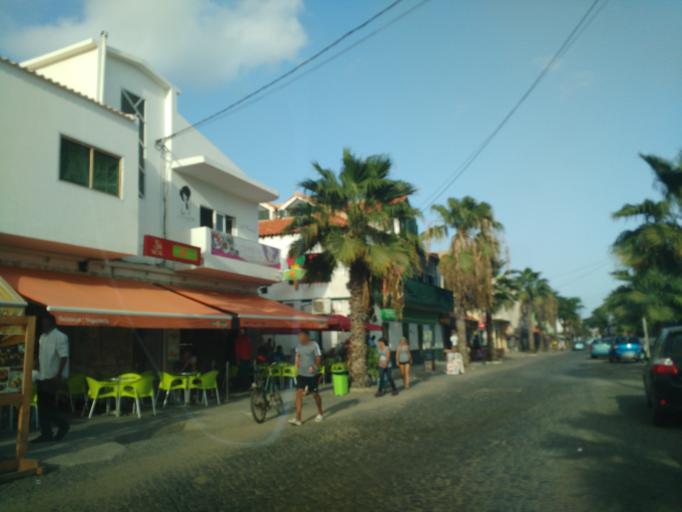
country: CV
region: Sal
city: Santa Maria
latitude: 16.5988
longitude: -22.9070
